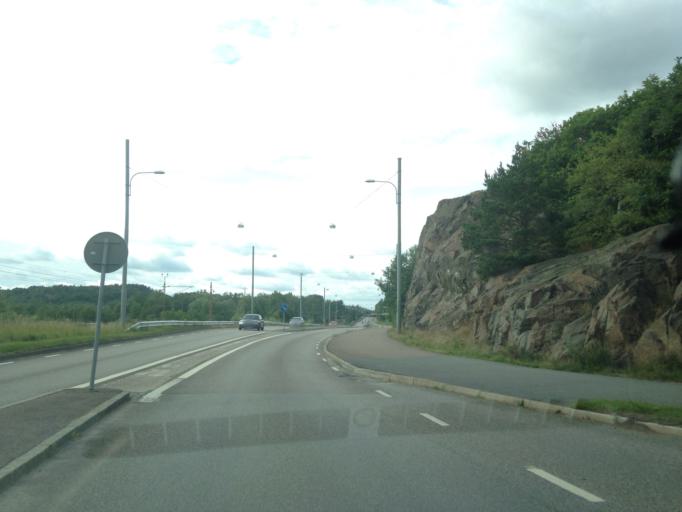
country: SE
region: Vaestra Goetaland
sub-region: Goteborg
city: Goeteborg
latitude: 57.7475
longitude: 11.9509
